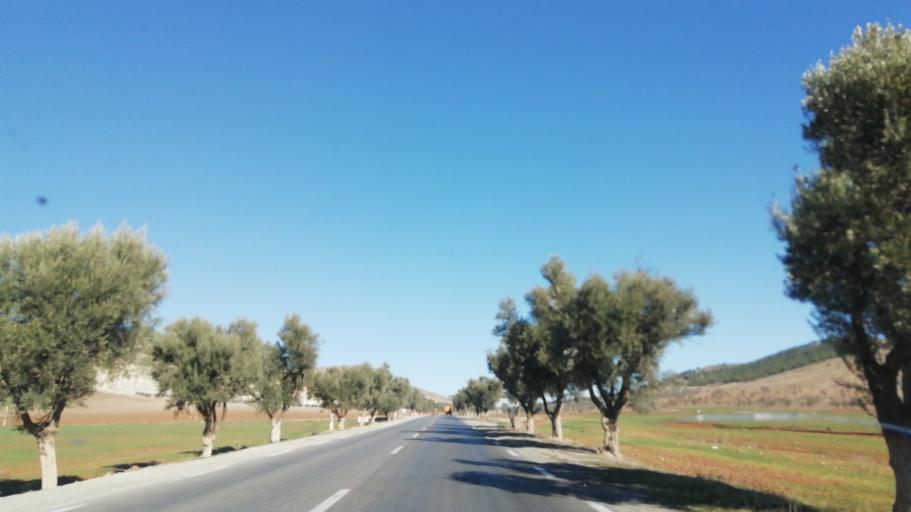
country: DZ
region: Mascara
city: Mascara
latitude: 35.2332
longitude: 0.1160
